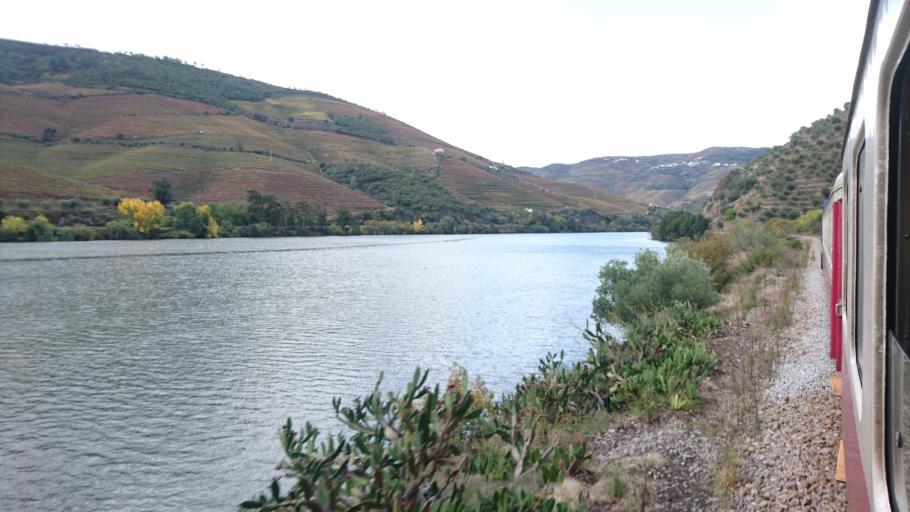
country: PT
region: Vila Real
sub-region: Sabrosa
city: Vilela
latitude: 41.1620
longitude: -7.6219
